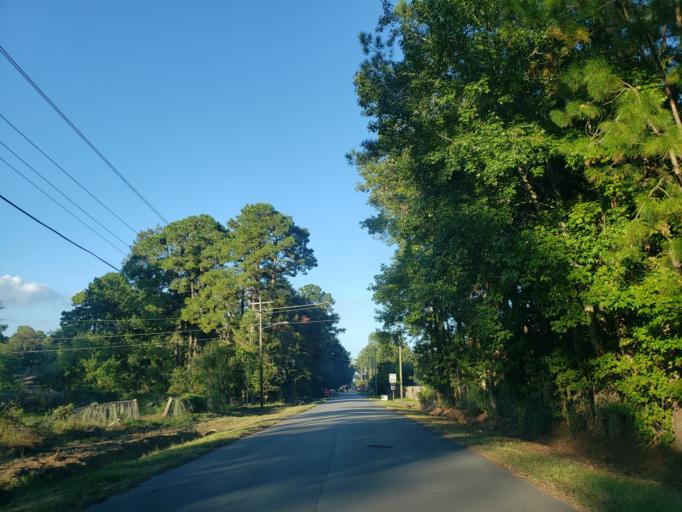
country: US
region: Georgia
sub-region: Chatham County
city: Isle of Hope
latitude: 31.9947
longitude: -81.0690
